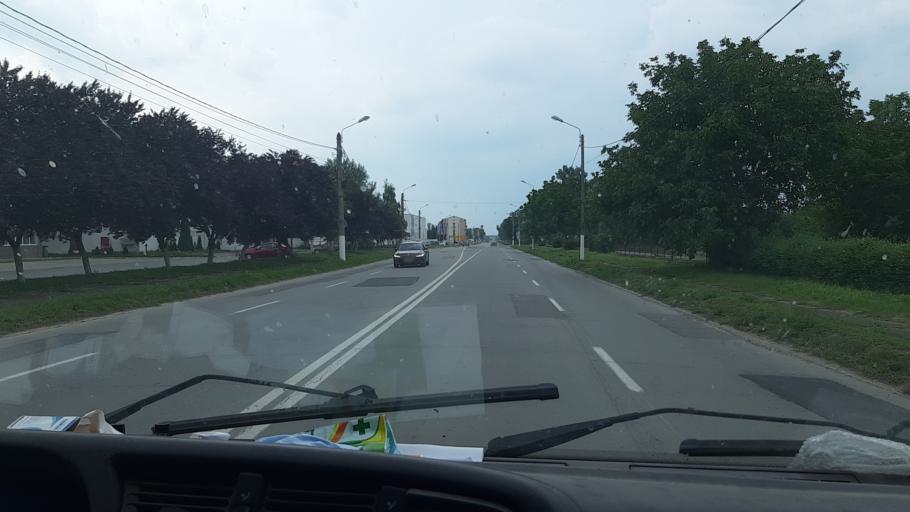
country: RO
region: Timis
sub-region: Municipiul Lugoj
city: Lugoj
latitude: 45.7051
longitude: 21.8902
